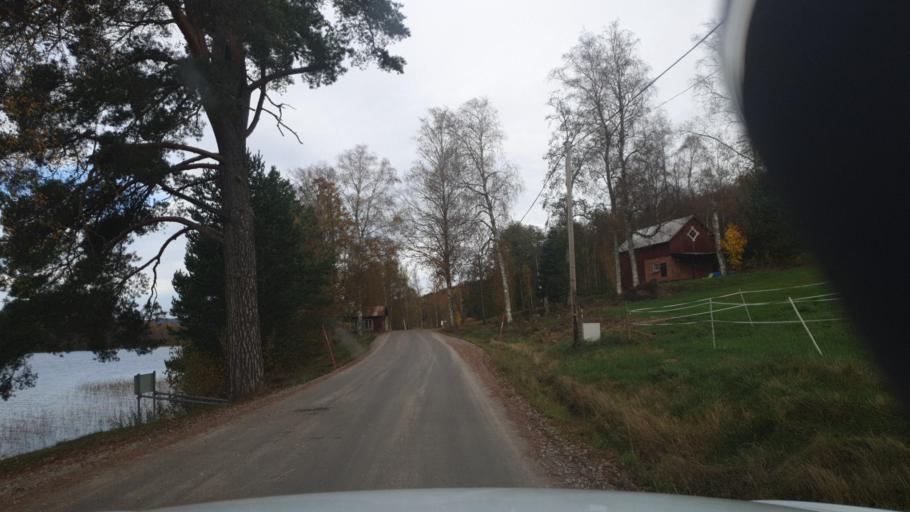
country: SE
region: Vaermland
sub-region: Arvika Kommun
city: Arvika
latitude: 59.7407
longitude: 12.8295
